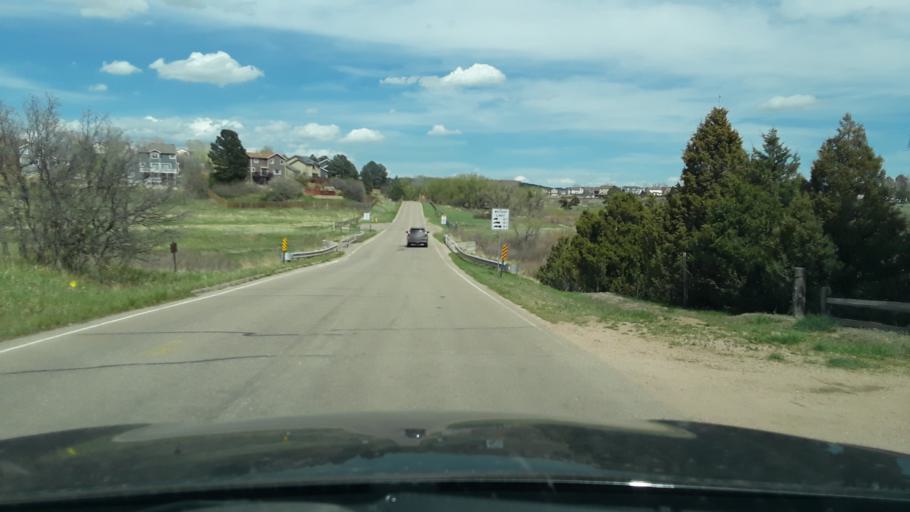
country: US
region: Colorado
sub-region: El Paso County
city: Monument
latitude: 39.0825
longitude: -104.8772
